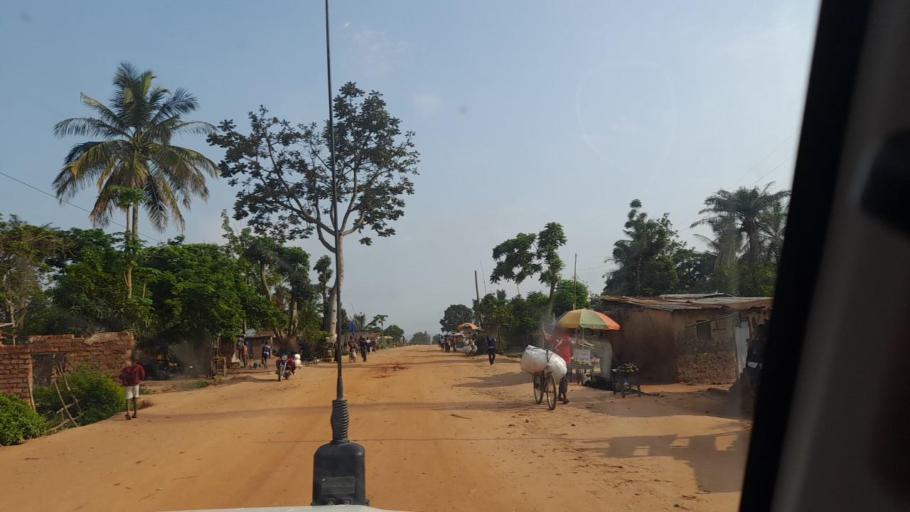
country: CD
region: Kasai-Occidental
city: Kananga
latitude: -5.8971
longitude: 22.3755
